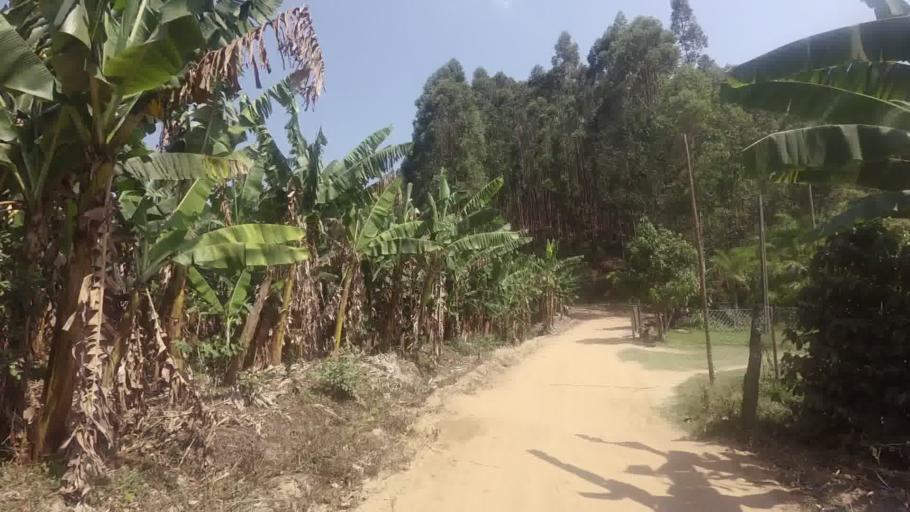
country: BR
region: Espirito Santo
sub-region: Mimoso Do Sul
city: Mimoso do Sul
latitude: -20.9990
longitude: -41.5029
